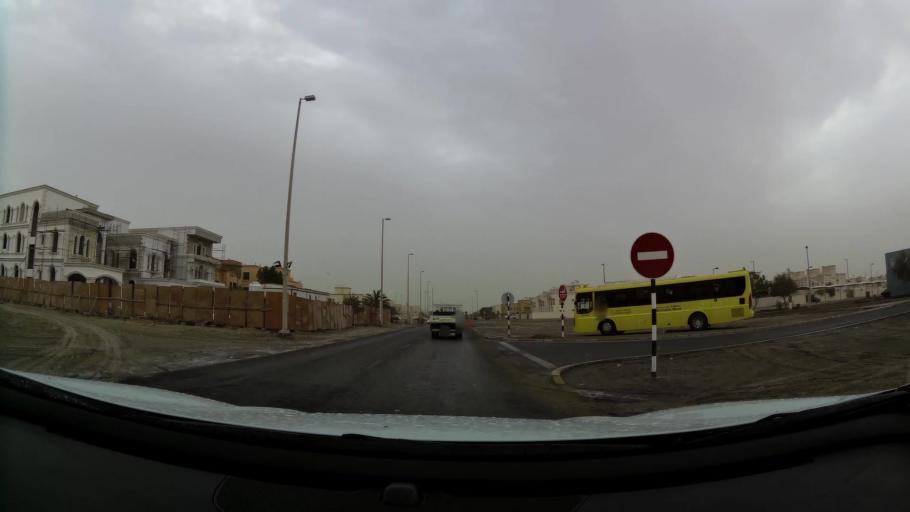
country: AE
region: Abu Dhabi
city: Abu Dhabi
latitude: 24.4111
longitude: 54.5867
